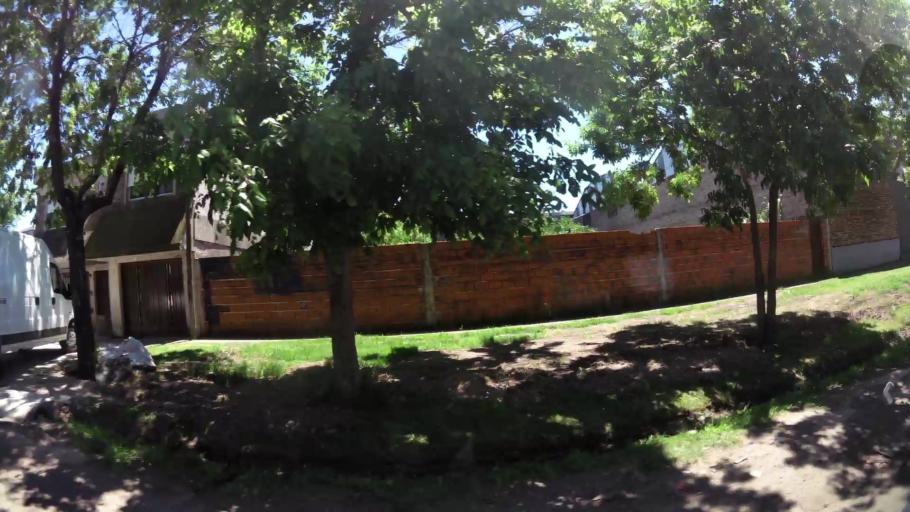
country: AR
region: Santa Fe
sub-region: Departamento de Rosario
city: Rosario
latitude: -32.9602
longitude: -60.7021
